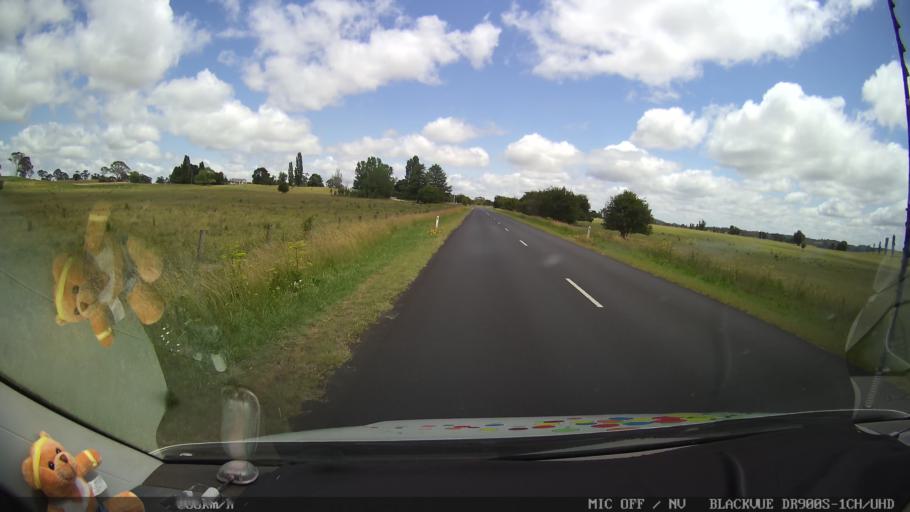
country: AU
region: New South Wales
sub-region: Glen Innes Severn
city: Glen Innes
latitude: -29.7054
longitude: 151.7201
